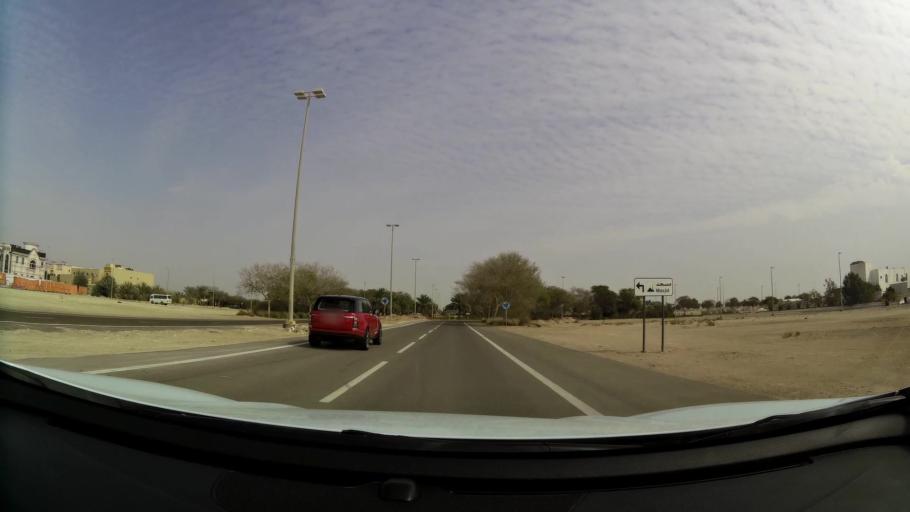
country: AE
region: Abu Dhabi
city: Abu Dhabi
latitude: 24.5806
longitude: 54.6937
